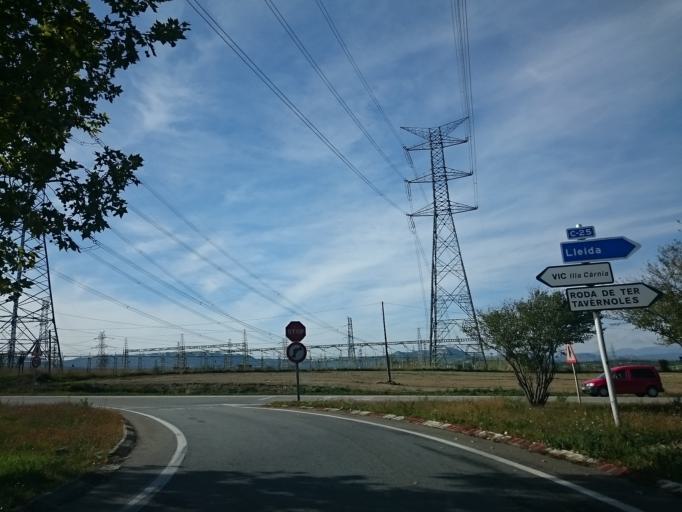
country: ES
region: Catalonia
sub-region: Provincia de Barcelona
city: Vic
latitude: 41.9567
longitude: 2.2845
